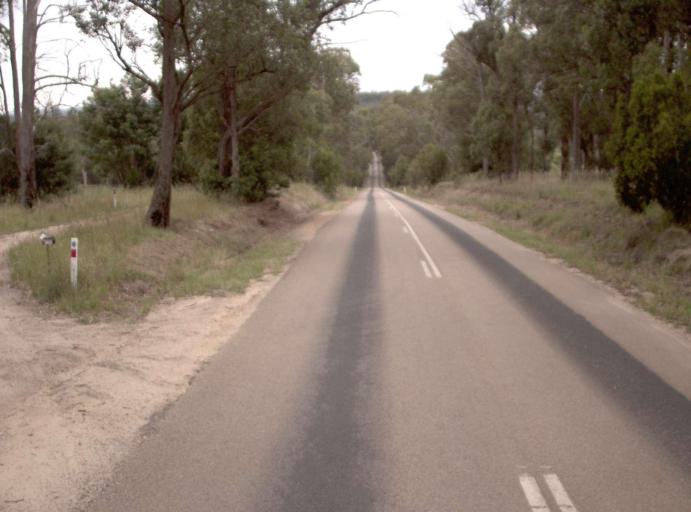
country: AU
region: Victoria
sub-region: East Gippsland
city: Bairnsdale
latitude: -37.7613
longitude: 147.5982
